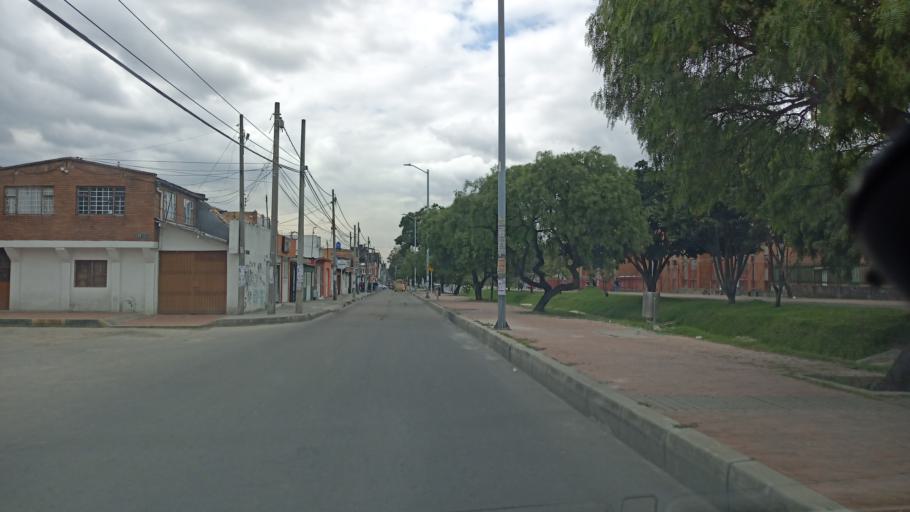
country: CO
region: Bogota D.C.
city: Bogota
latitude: 4.5747
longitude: -74.1080
